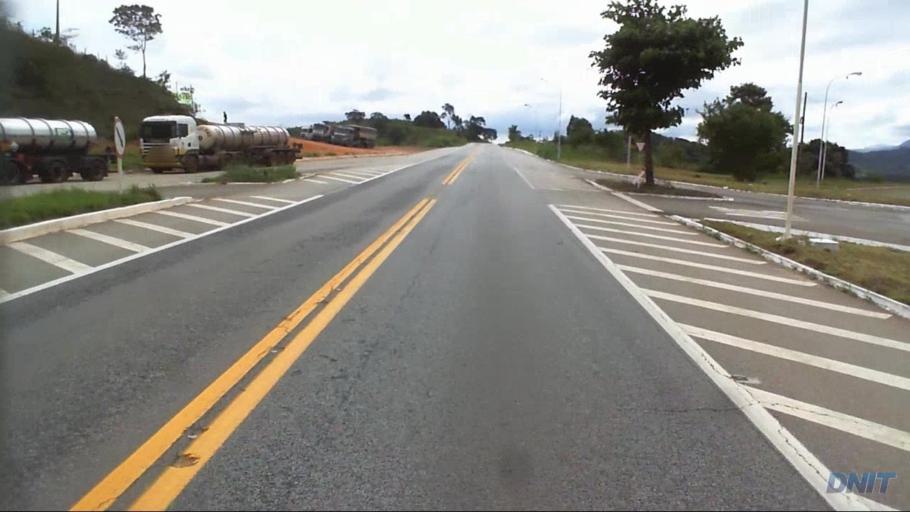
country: BR
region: Minas Gerais
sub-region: Caete
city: Caete
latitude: -19.7379
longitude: -43.5574
